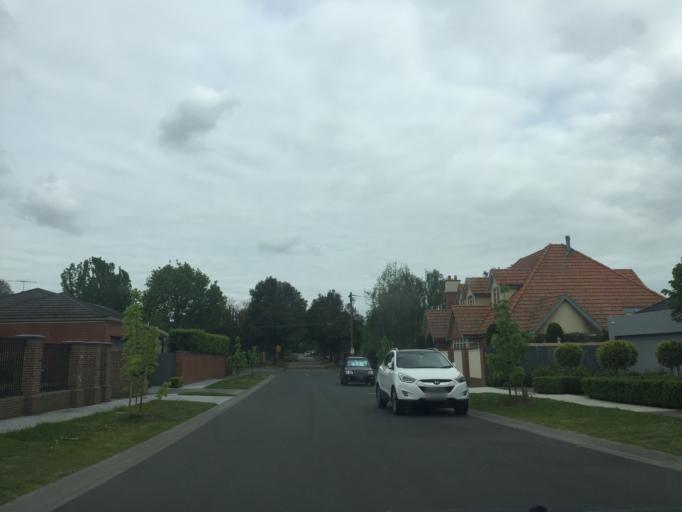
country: AU
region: Victoria
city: Balwyn
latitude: -37.8184
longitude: 145.0634
